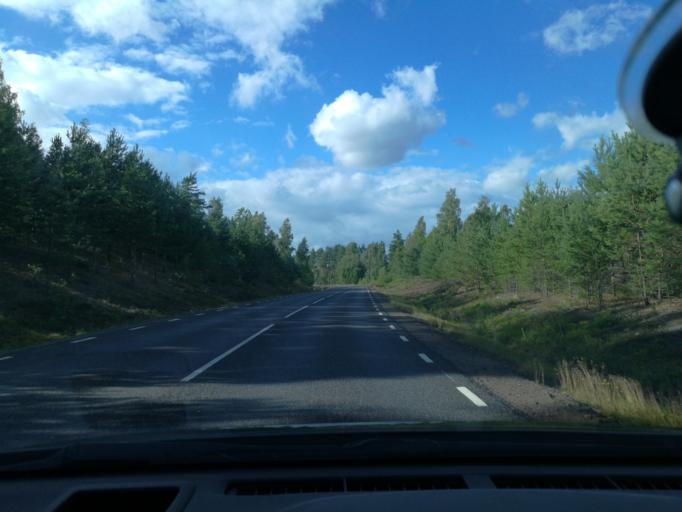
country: SE
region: Kronoberg
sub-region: Vaxjo Kommun
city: Braas
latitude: 57.0565
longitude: 15.0385
